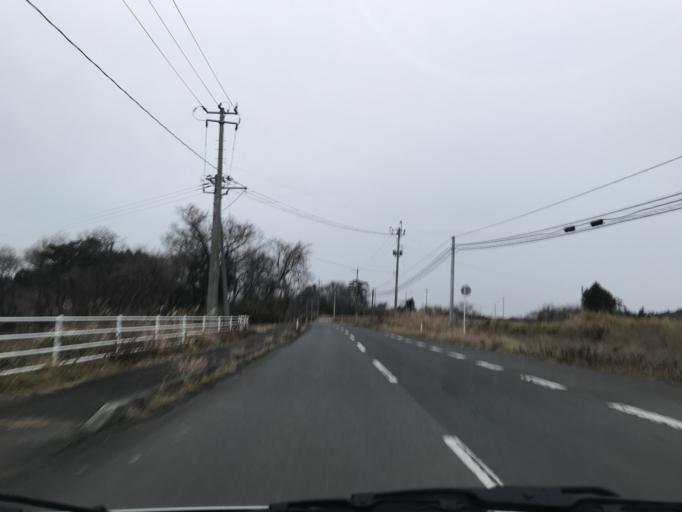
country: JP
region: Miyagi
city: Kogota
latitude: 38.6961
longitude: 141.0953
